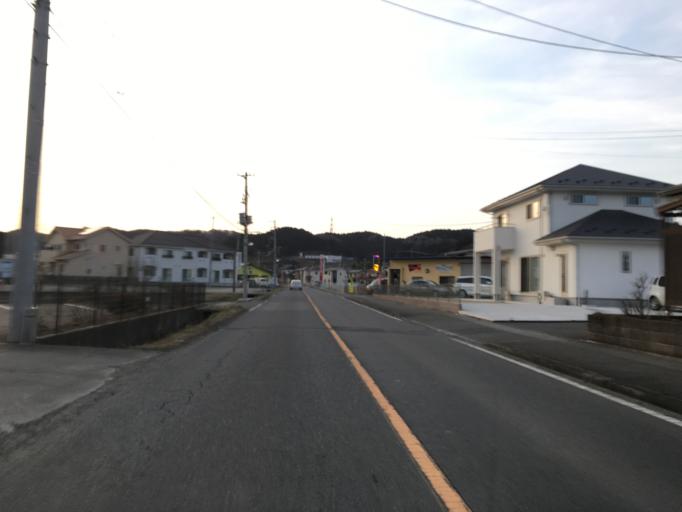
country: JP
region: Fukushima
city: Ishikawa
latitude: 37.0279
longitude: 140.3807
